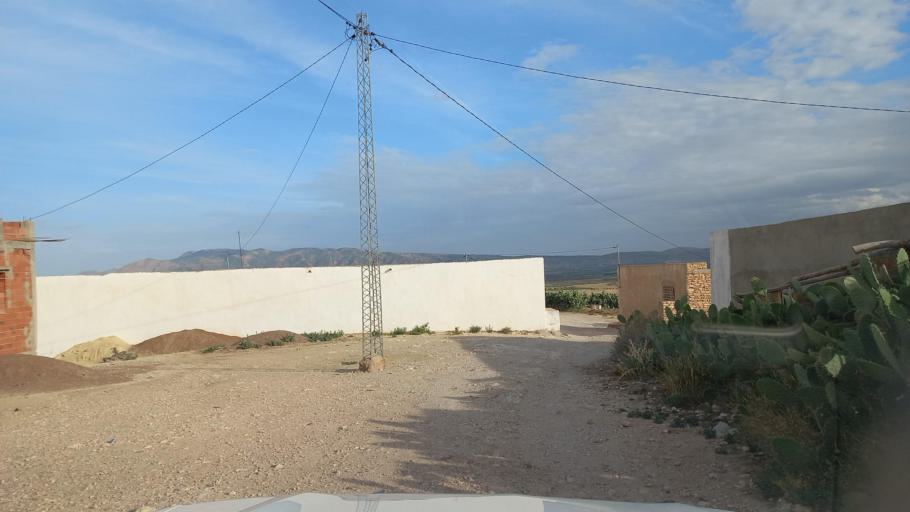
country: TN
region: Al Qasrayn
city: Sbiba
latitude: 35.4538
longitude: 9.0868
